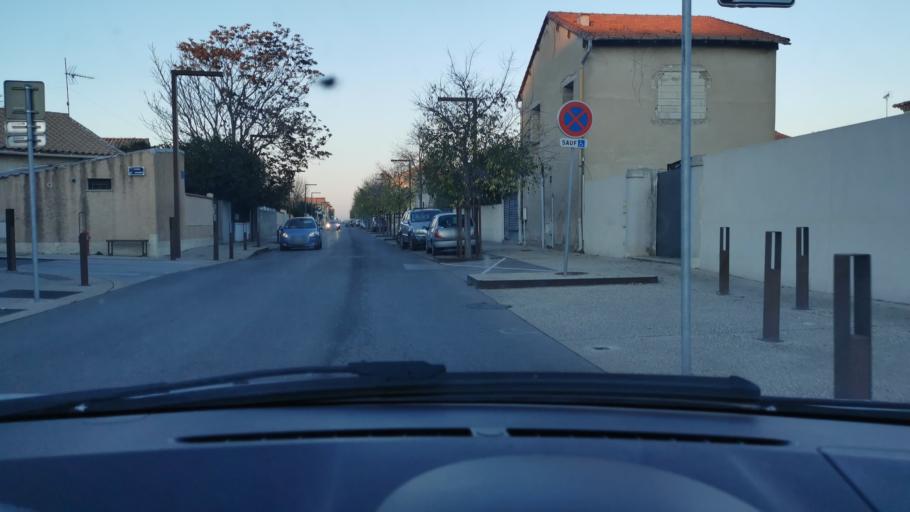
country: FR
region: Languedoc-Roussillon
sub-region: Departement de l'Herault
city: Frontignan
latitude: 43.4493
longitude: 3.7571
